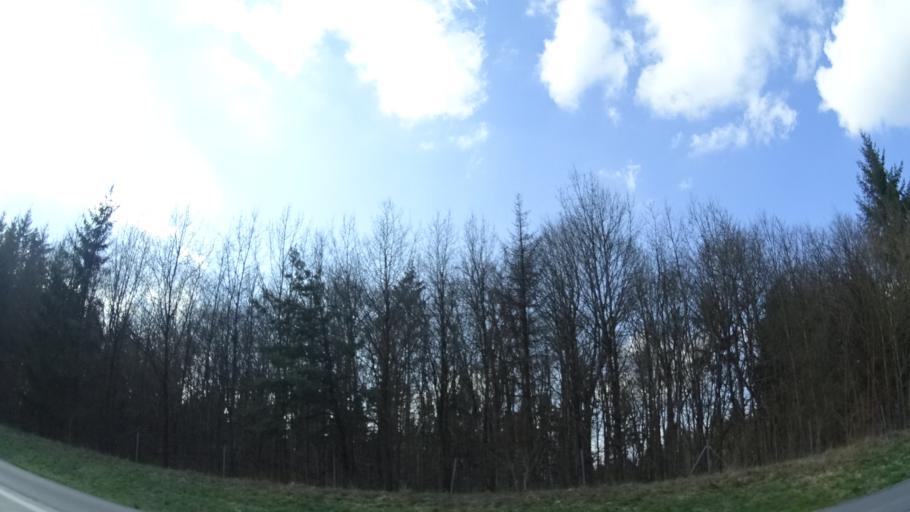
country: DE
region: Baden-Wuerttemberg
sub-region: Karlsruhe Region
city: Rosenberg
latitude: 49.4442
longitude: 9.5161
